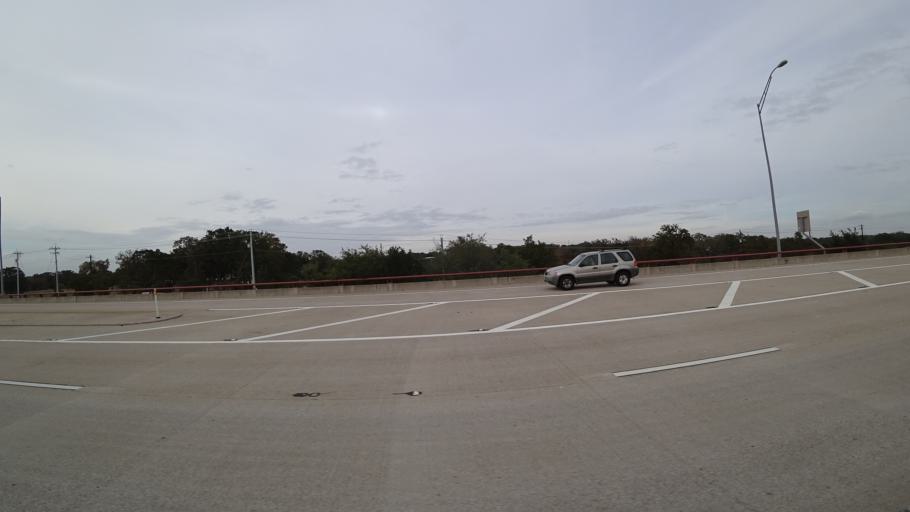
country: US
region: Texas
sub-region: Williamson County
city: Brushy Creek
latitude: 30.4814
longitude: -97.7466
